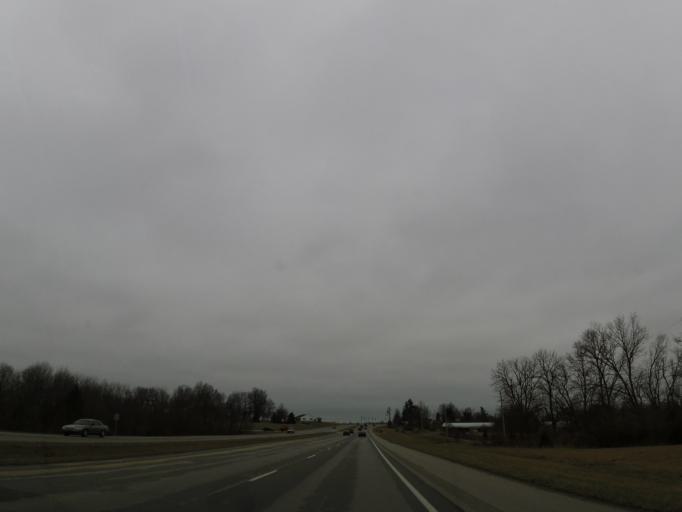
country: US
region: Kentucky
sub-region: Anderson County
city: Lawrenceburg
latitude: 38.1164
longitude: -84.9147
